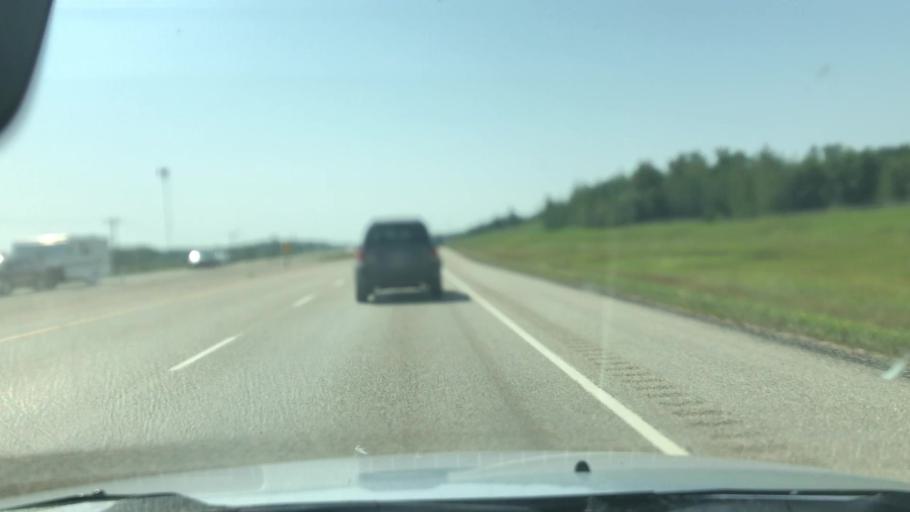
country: CA
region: Alberta
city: Devon
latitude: 53.4510
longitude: -113.7629
